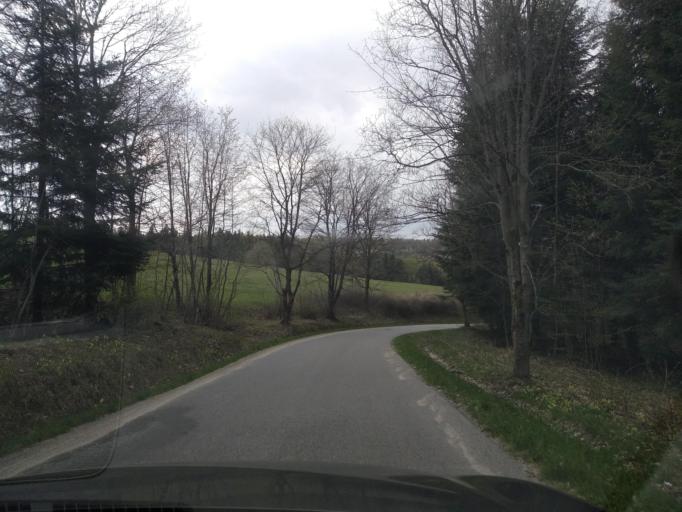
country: PL
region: Subcarpathian Voivodeship
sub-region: Powiat leski
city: Baligrod
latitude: 49.3580
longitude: 22.2248
